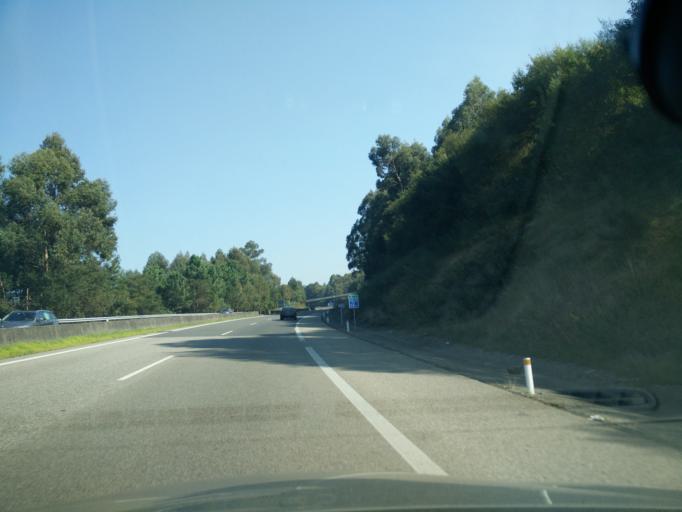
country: ES
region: Galicia
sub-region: Provincia da Coruna
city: Mino
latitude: 43.3637
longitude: -8.2002
